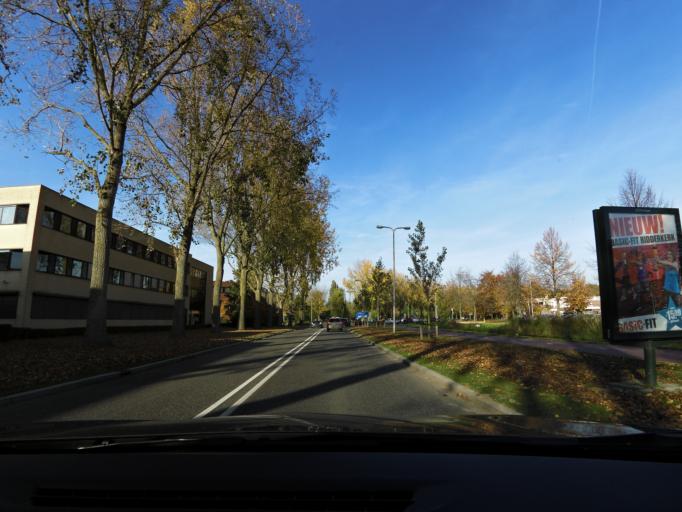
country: NL
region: South Holland
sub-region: Gemeente Ridderkerk
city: Ridderkerk
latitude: 51.8774
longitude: 4.5900
